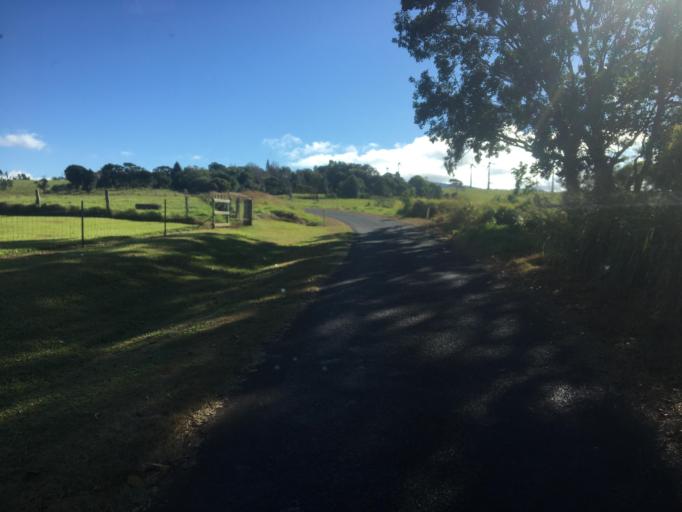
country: AU
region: Queensland
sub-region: Tablelands
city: Ravenshoe
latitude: -17.6008
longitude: 145.5233
